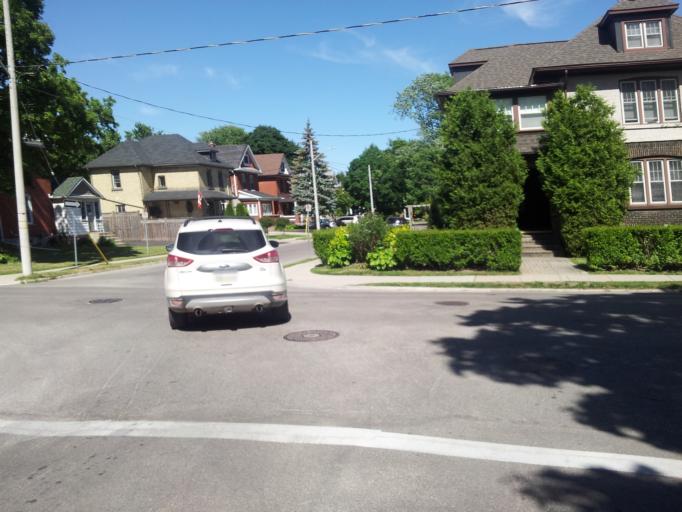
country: CA
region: Ontario
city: Stratford
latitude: 43.3703
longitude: -80.9737
